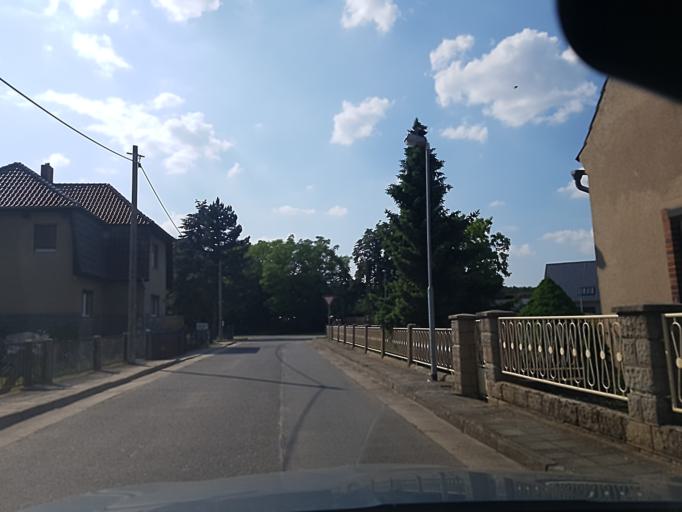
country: DE
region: Brandenburg
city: Bad Liebenwerda
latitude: 51.5339
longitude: 13.4402
